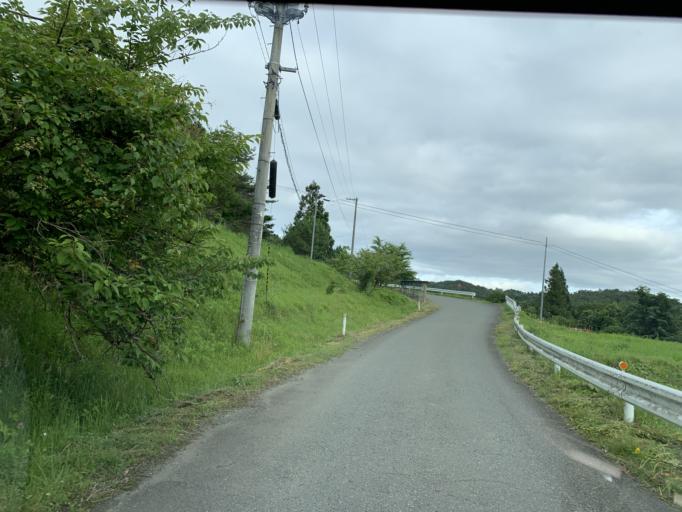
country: JP
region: Iwate
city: Ichinoseki
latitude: 38.8257
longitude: 141.2318
